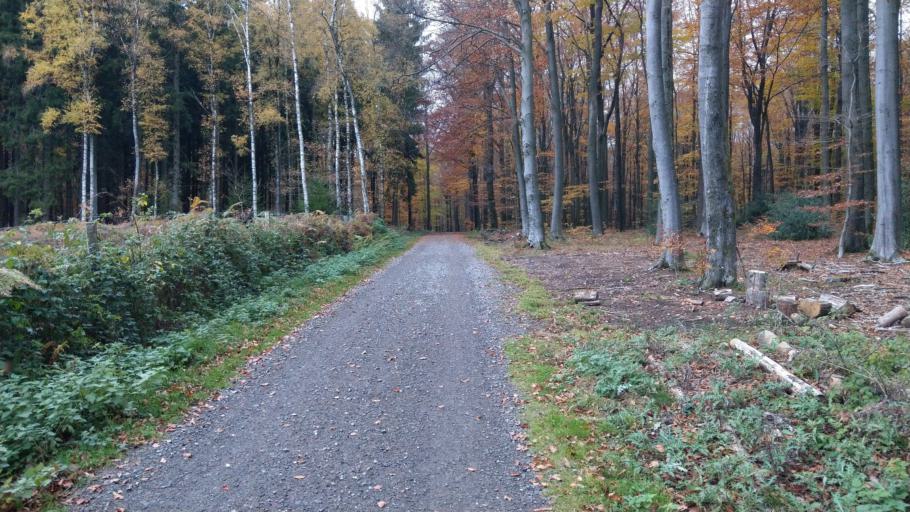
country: NL
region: Limburg
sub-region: Gemeente Vaals
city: Vaals
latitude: 50.7434
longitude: 6.0336
